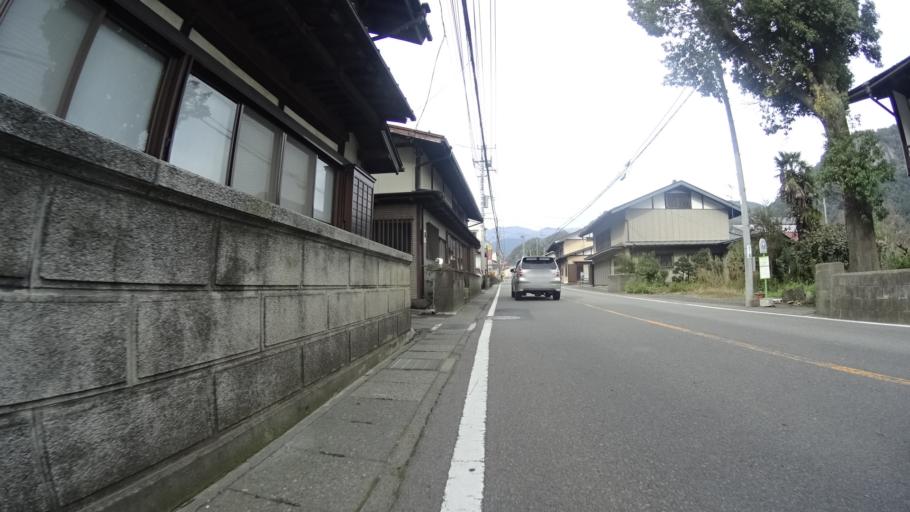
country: JP
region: Yamanashi
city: Otsuki
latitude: 35.6133
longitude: 138.9520
